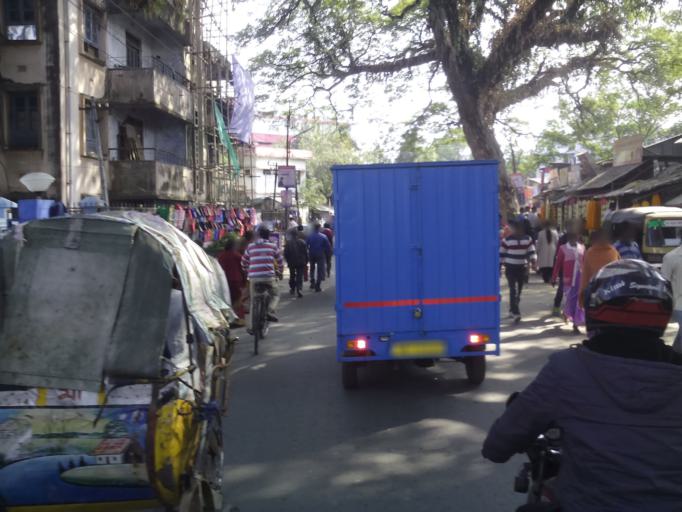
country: IN
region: West Bengal
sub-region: Darjiling
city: Shiliguri
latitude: 26.7102
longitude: 88.4280
